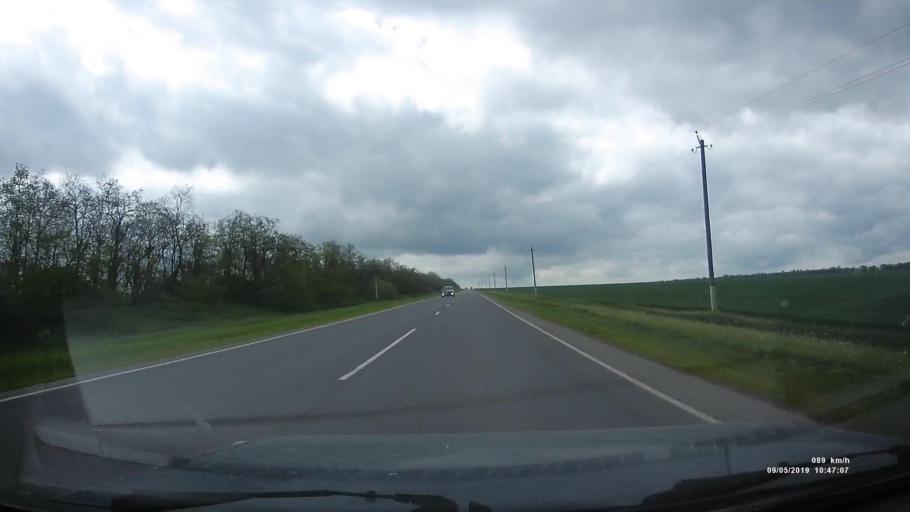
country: RU
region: Rostov
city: Peshkovo
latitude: 46.9753
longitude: 39.3557
